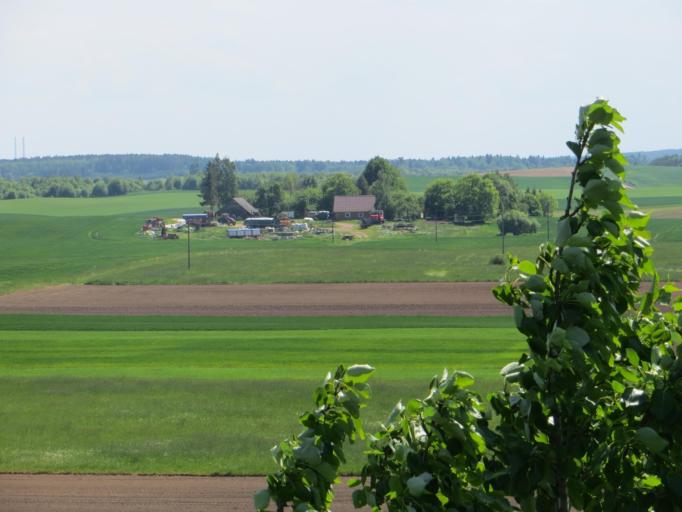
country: LT
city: Kaisiadorys
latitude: 54.9042
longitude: 24.5416
